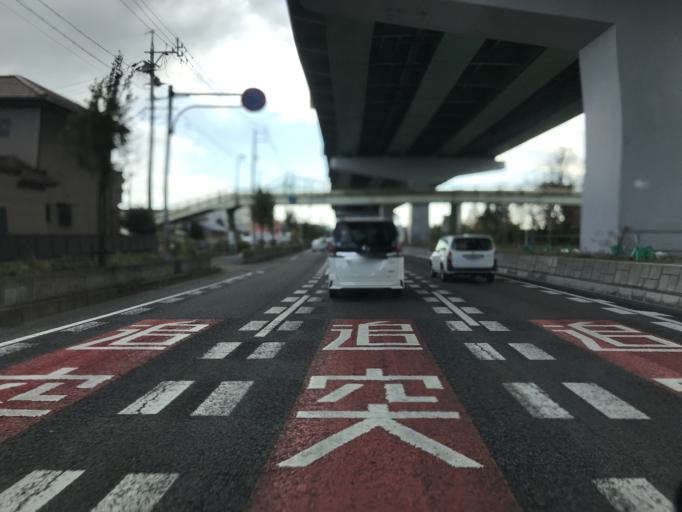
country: JP
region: Aichi
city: Komaki
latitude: 35.2693
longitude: 136.9076
